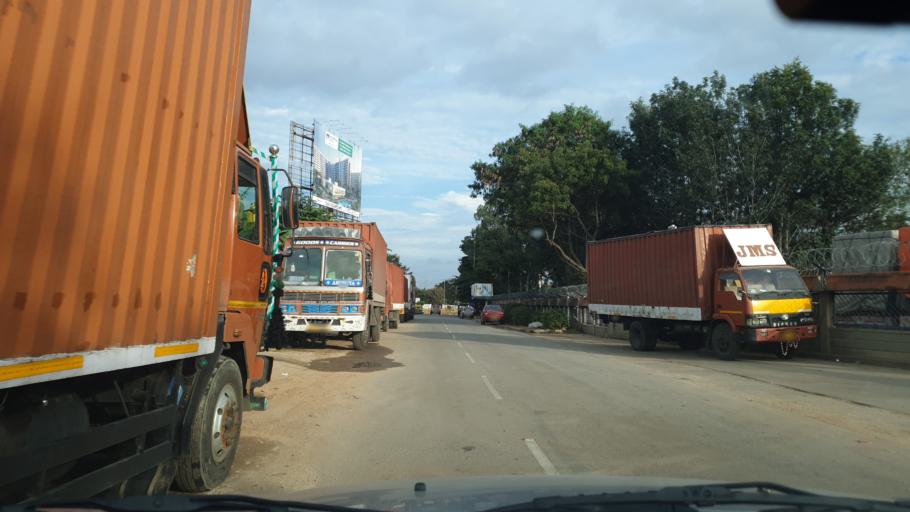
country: IN
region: Karnataka
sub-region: Bangalore Rural
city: Devanhalli
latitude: 13.1888
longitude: 77.6430
